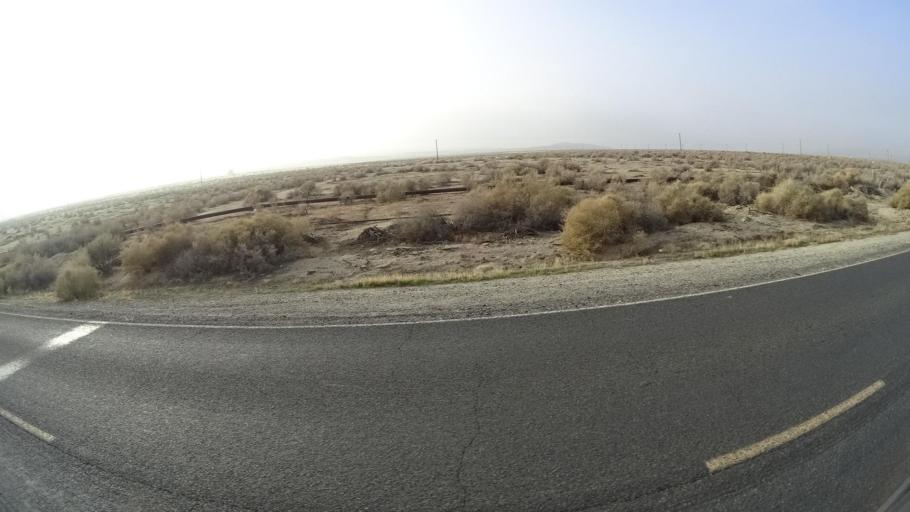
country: US
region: California
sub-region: Kern County
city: Ford City
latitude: 35.2152
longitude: -119.4455
